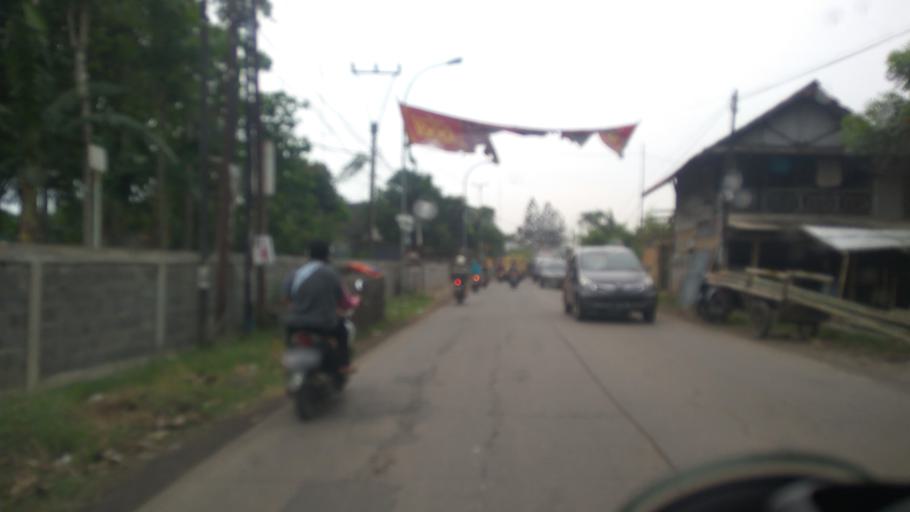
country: ID
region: West Java
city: Bekasi
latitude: -6.2047
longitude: 107.0325
